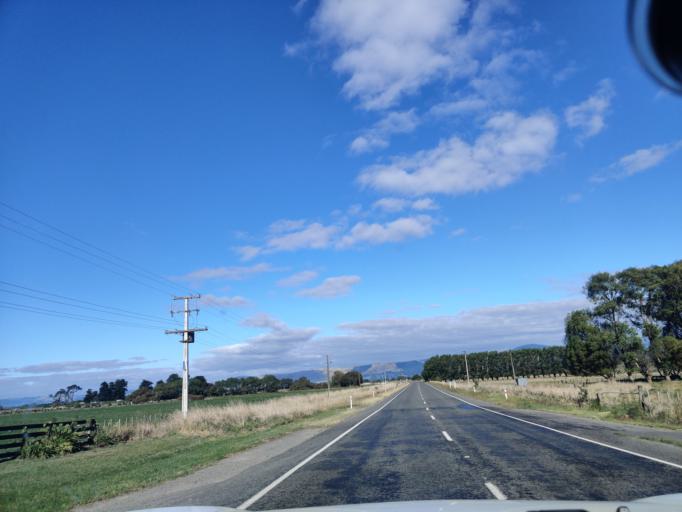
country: NZ
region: Manawatu-Wanganui
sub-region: Horowhenua District
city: Foxton
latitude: -40.4232
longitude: 175.4488
